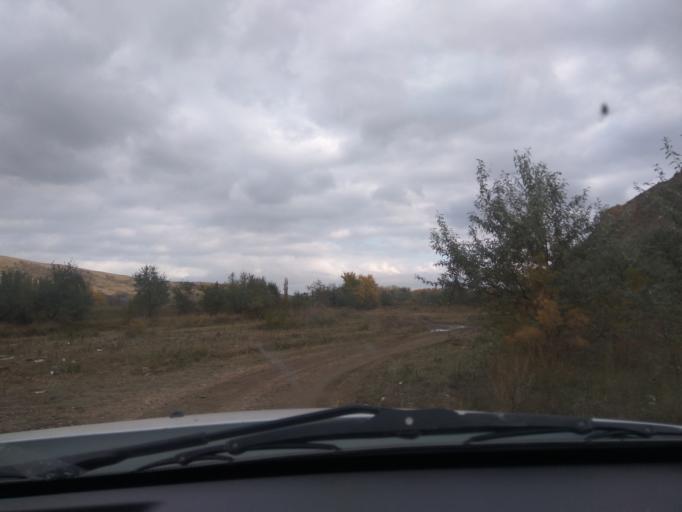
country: RU
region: Dagestan
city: Korkmaskala
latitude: 42.9997
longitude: 47.2388
